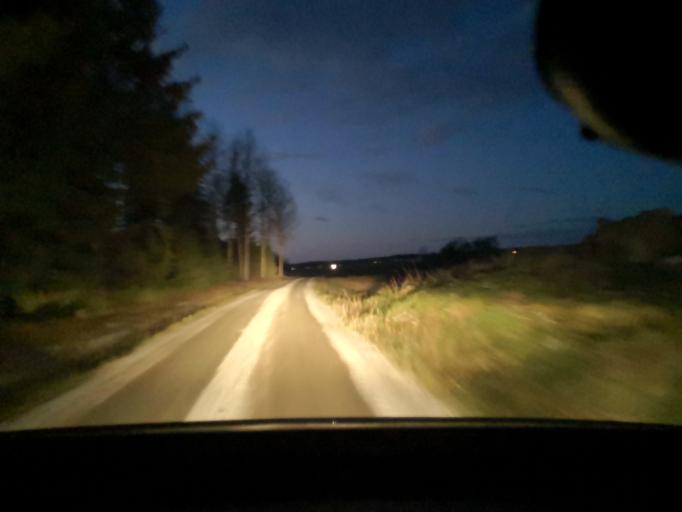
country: SE
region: Uppsala
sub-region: Heby Kommun
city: Heby
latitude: 59.9150
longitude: 16.7506
